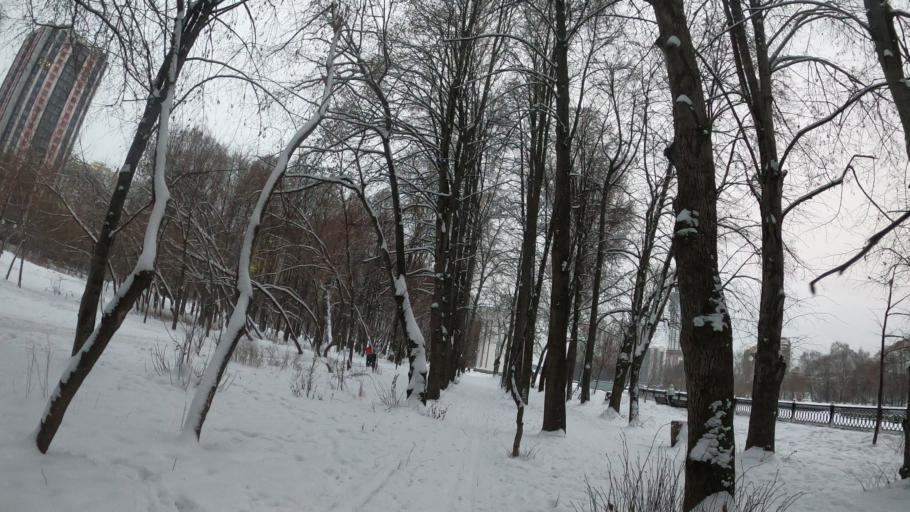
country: RU
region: Moskovskaya
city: Levoberezhnaya
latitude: 55.9030
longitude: 37.4709
